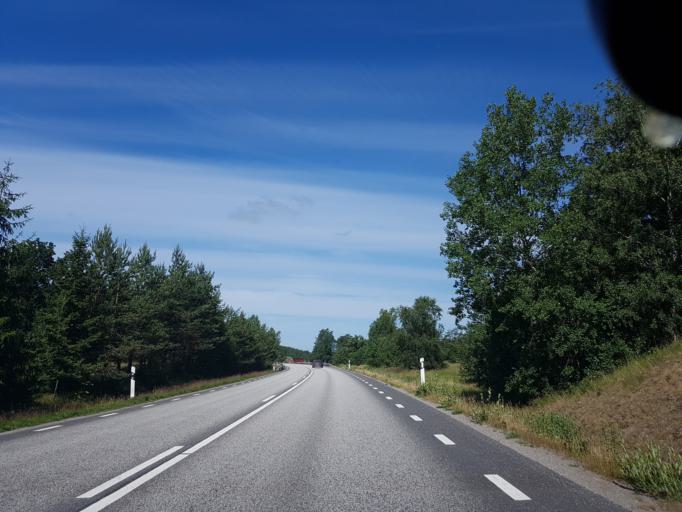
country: SE
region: Vaestra Goetaland
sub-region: Orust
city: Henan
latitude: 58.1458
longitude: 11.6313
